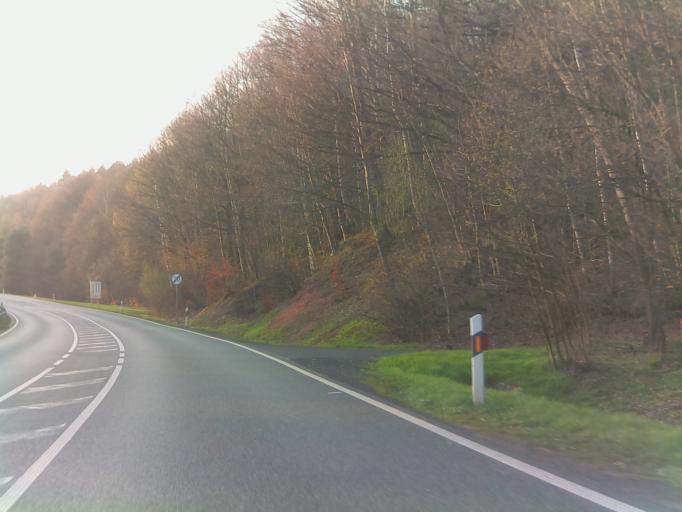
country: DE
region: Hesse
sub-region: Regierungsbezirk Kassel
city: Friedewald
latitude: 50.8675
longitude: 9.9052
